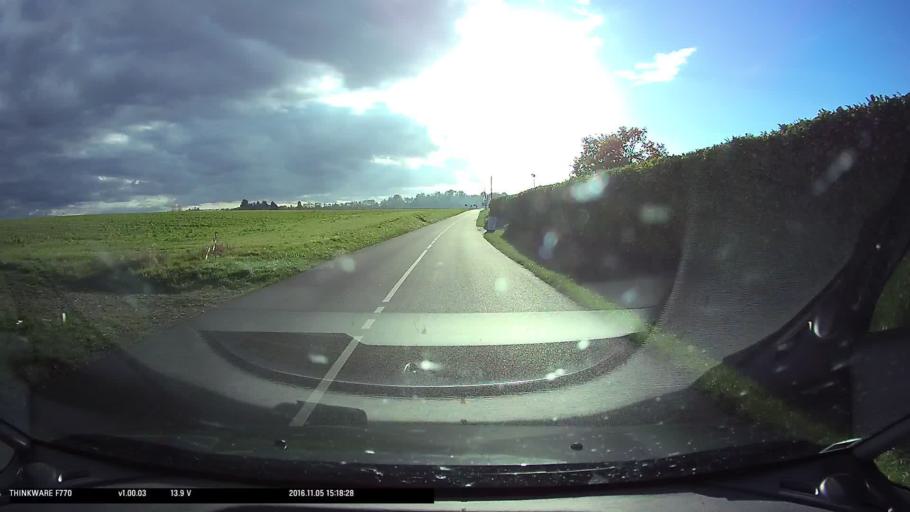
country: FR
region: Ile-de-France
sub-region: Departement du Val-d'Oise
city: Ableiges
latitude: 49.0761
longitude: 1.9710
